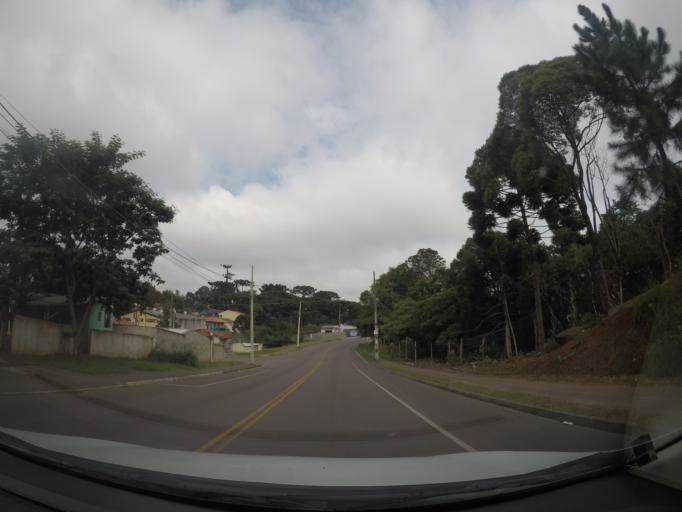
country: BR
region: Parana
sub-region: Colombo
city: Colombo
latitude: -25.3454
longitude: -49.2233
